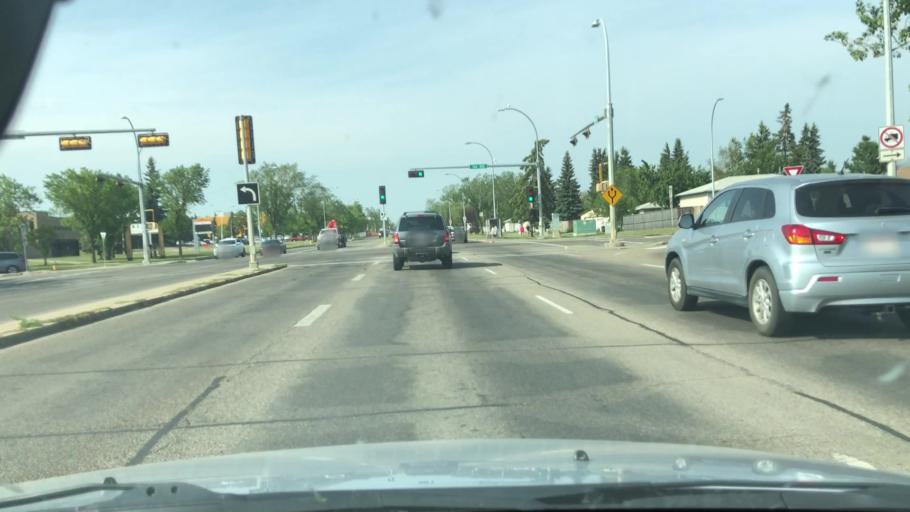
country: CA
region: Alberta
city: Edmonton
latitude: 53.6040
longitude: -113.4428
